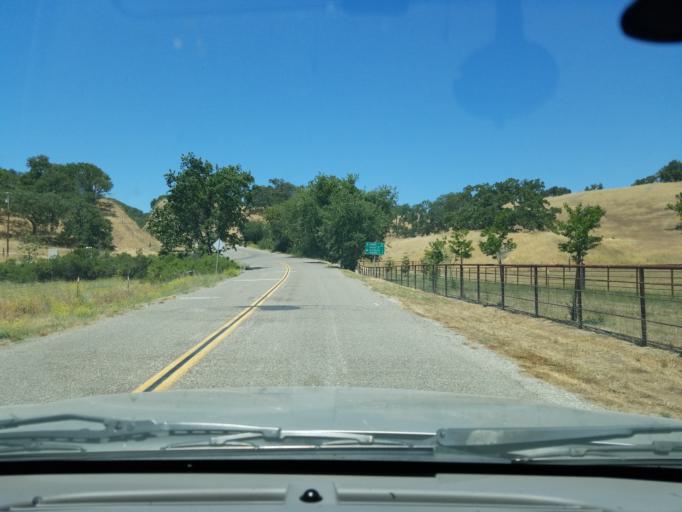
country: US
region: California
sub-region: Monterey County
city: Gonzales
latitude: 36.4013
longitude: -121.5799
